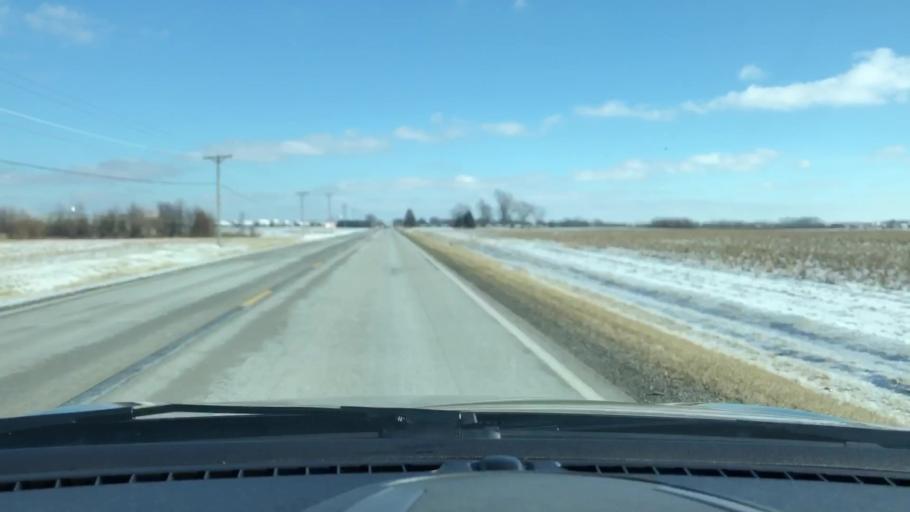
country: US
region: Illinois
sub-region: Will County
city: Ingalls Park
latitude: 41.4822
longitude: -88.0164
